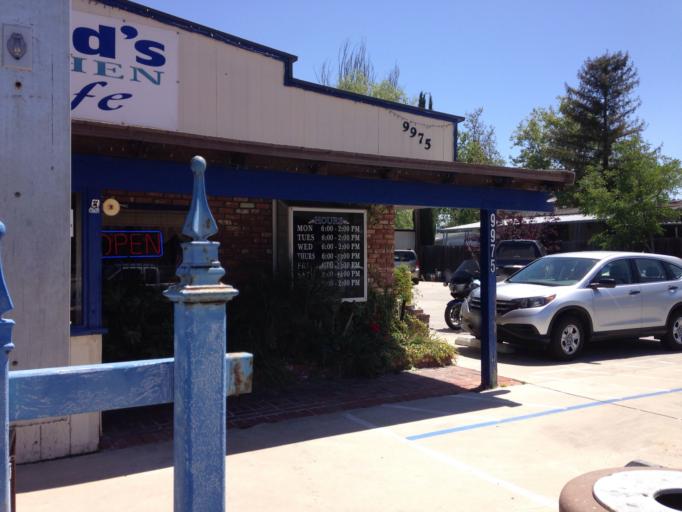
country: US
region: California
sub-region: San Luis Obispo County
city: Atascadero
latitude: 35.4636
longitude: -120.6463
